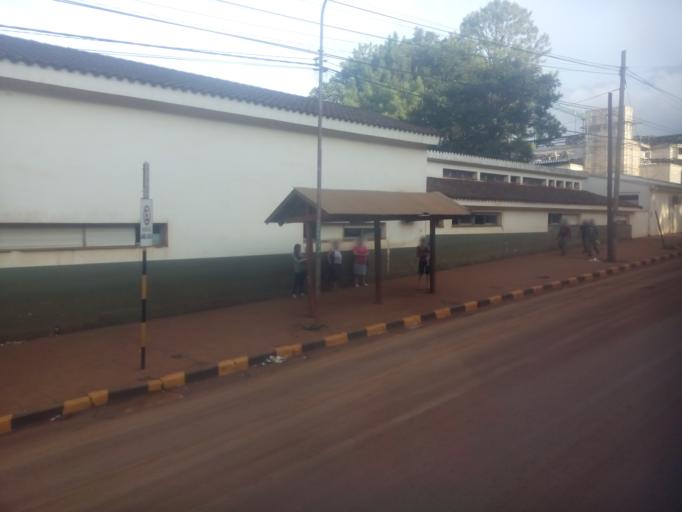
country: AR
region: Misiones
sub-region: Departamento de Obera
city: Obera
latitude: -27.4914
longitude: -55.1455
